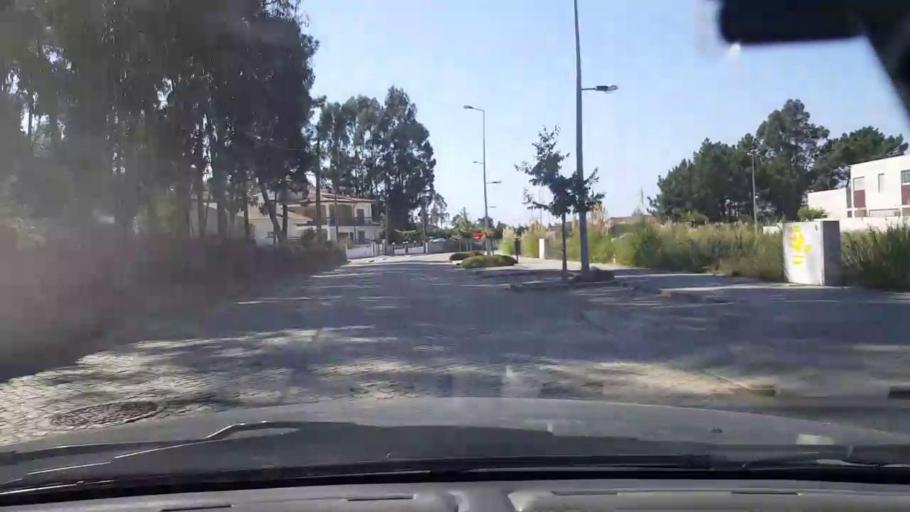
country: PT
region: Porto
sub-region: Matosinhos
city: Lavra
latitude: 41.2946
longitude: -8.7133
